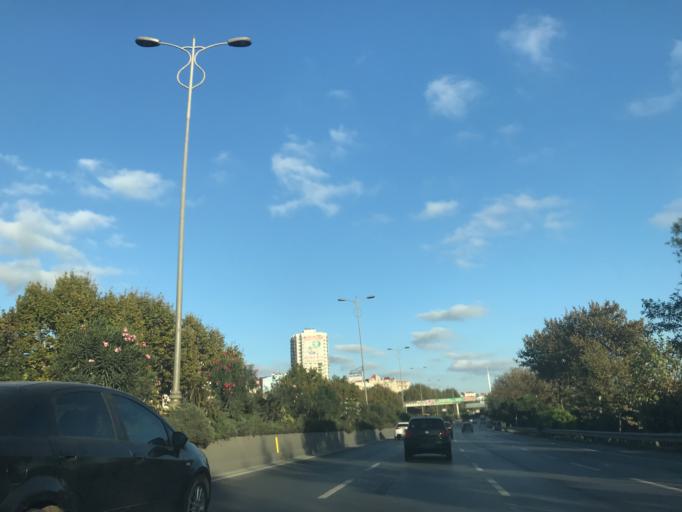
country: TR
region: Istanbul
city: Bagcilar
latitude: 41.0537
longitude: 28.8635
